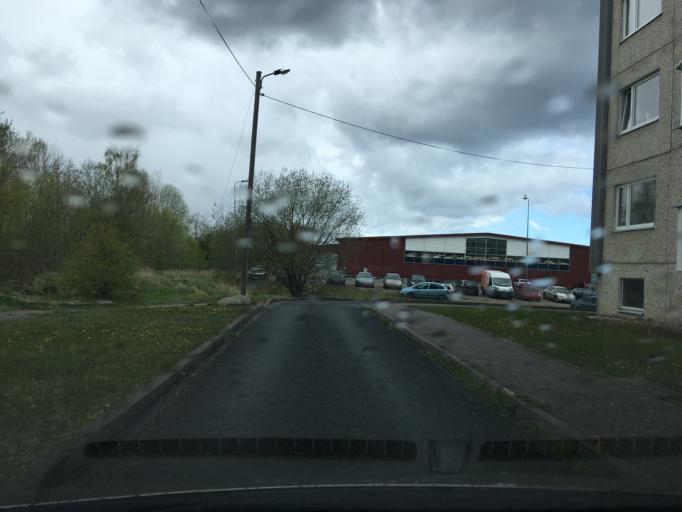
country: EE
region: Harju
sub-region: Tallinna linn
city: Kose
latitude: 59.4482
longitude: 24.8470
